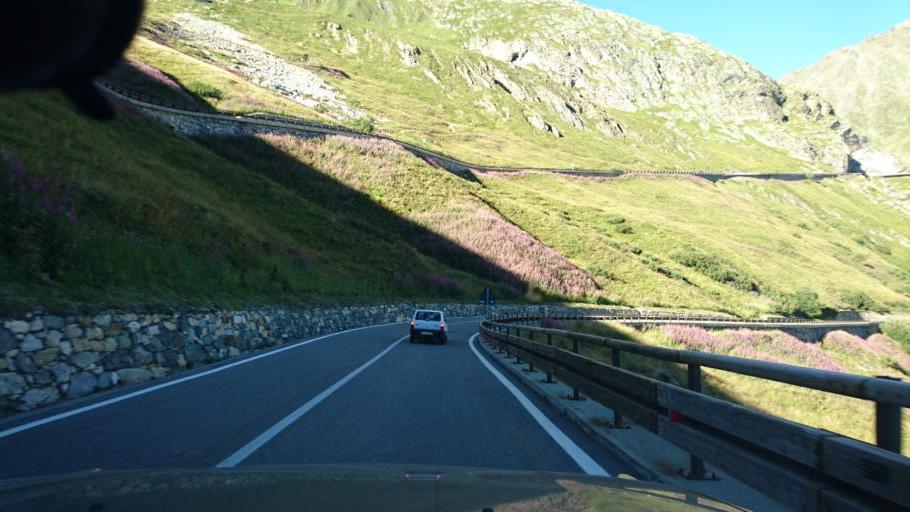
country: IT
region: Aosta Valley
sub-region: Valle d'Aosta
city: San Leonardo
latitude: 45.8566
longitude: 7.1453
